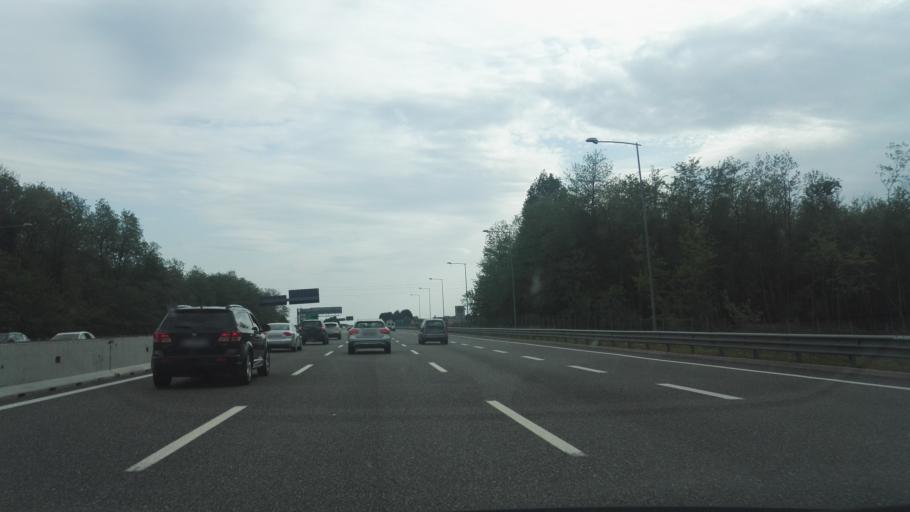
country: IT
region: Lombardy
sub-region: Provincia di Como
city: Cirimido
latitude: 45.7074
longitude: 9.0220
